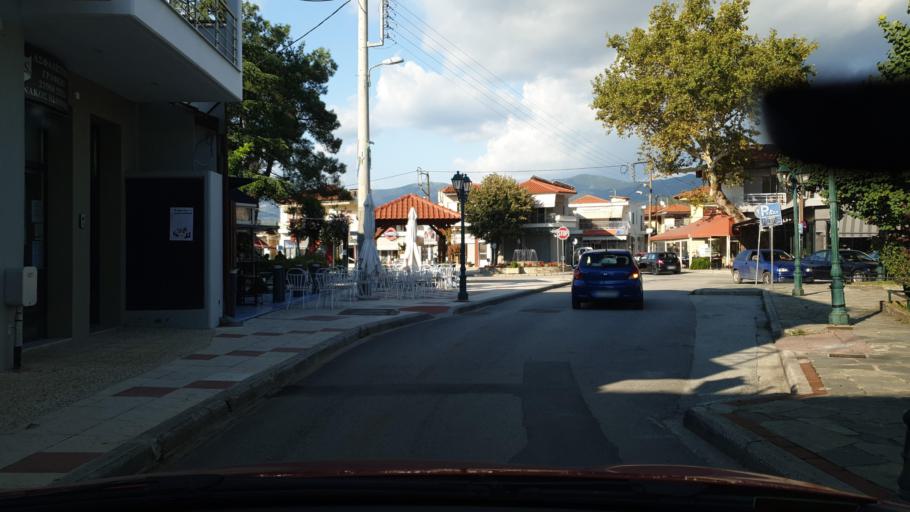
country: GR
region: Central Macedonia
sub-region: Nomos Thessalonikis
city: Vasilika
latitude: 40.4801
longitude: 23.1366
